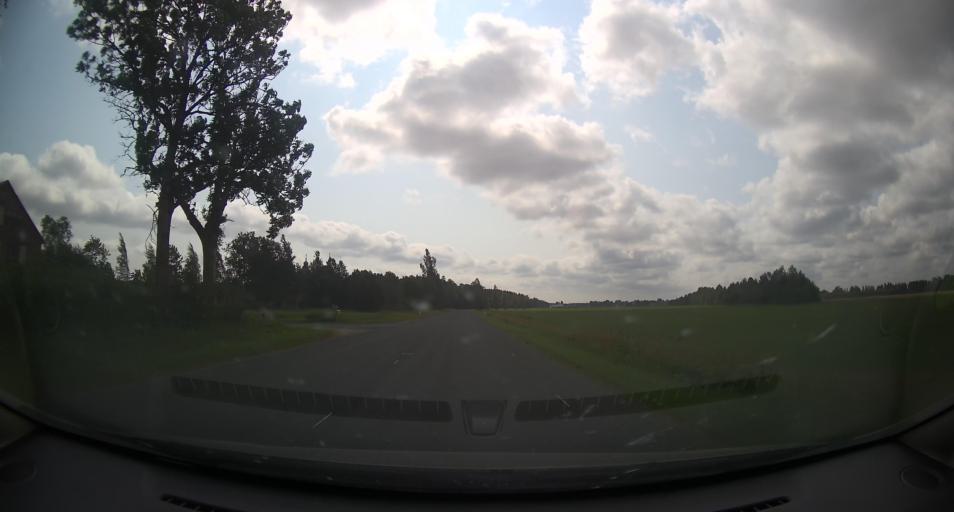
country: EE
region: Paernumaa
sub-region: Audru vald
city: Audru
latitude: 58.4881
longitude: 24.3355
